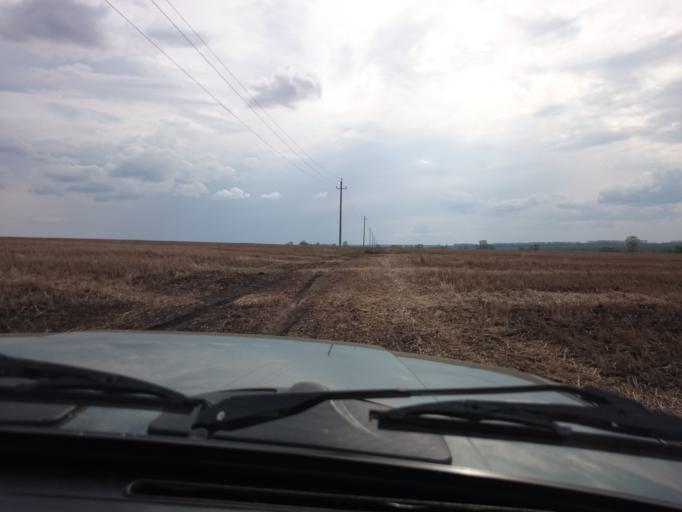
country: RU
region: Mordoviya
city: Kadoshkino
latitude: 54.0203
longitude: 44.4688
